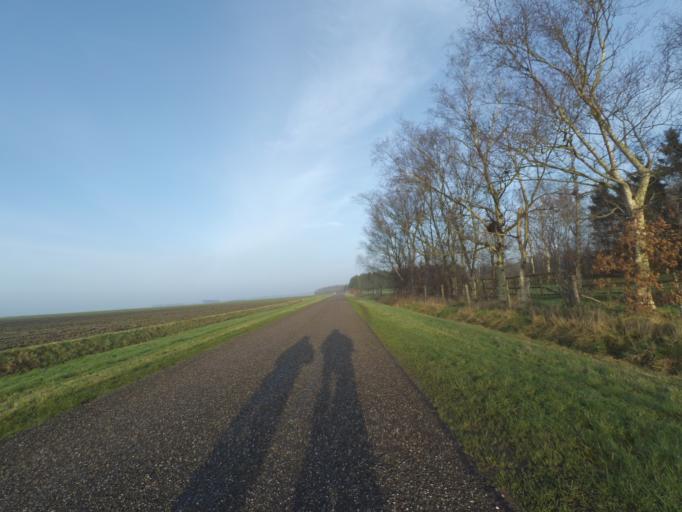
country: NL
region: Drenthe
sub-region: Gemeente Borger-Odoorn
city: Borger
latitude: 52.8844
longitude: 6.8226
